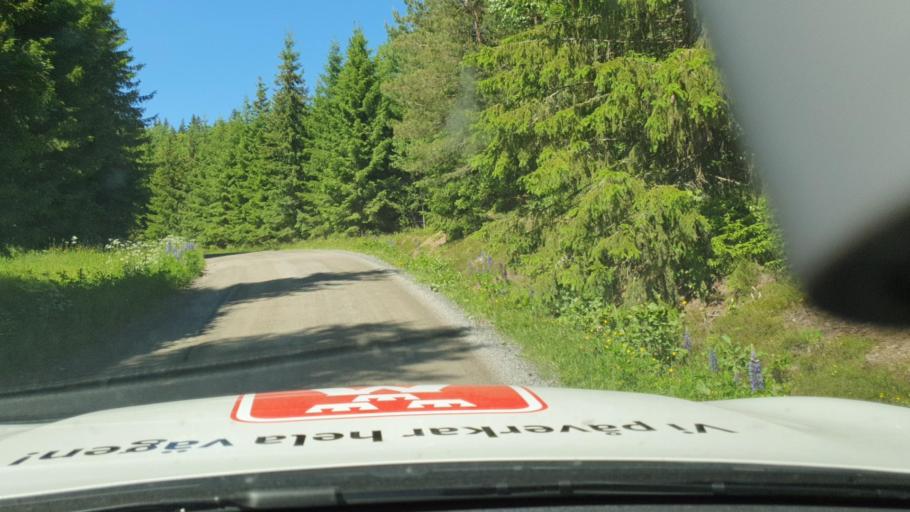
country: SE
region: Joenkoeping
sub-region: Mullsjo Kommun
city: Mullsjoe
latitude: 57.8921
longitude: 13.9548
